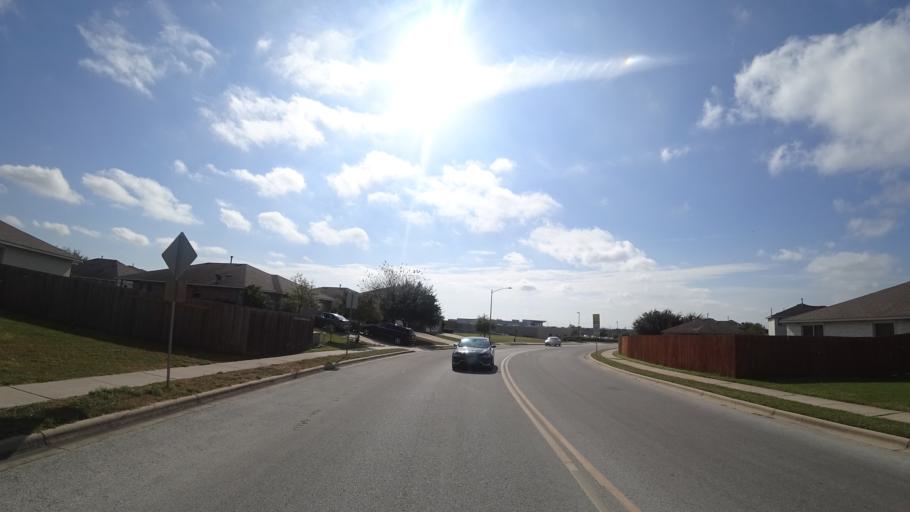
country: US
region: Texas
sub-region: Travis County
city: Pflugerville
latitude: 30.4243
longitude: -97.6398
